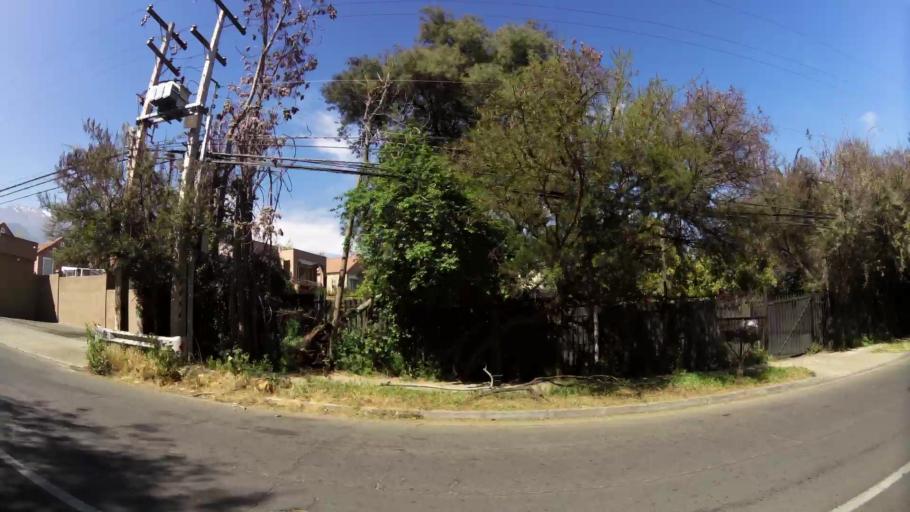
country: CL
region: Santiago Metropolitan
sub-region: Provincia de Santiago
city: Villa Presidente Frei, Nunoa, Santiago, Chile
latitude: -33.4323
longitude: -70.5288
